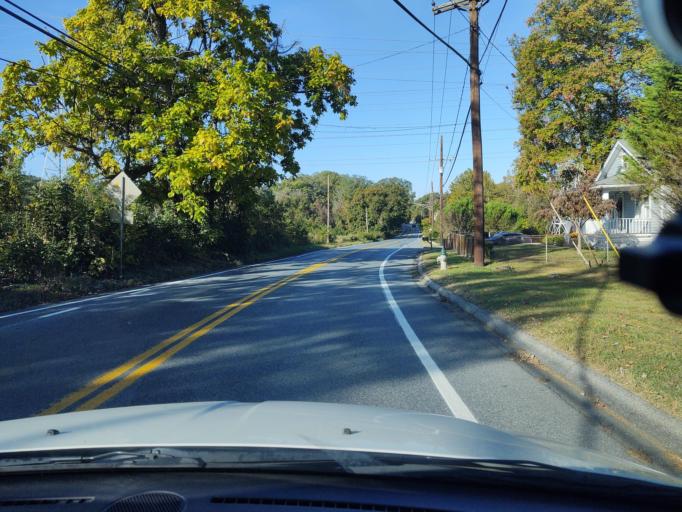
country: US
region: Maryland
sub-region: Prince George's County
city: Glenn Dale
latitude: 39.0068
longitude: -76.7666
